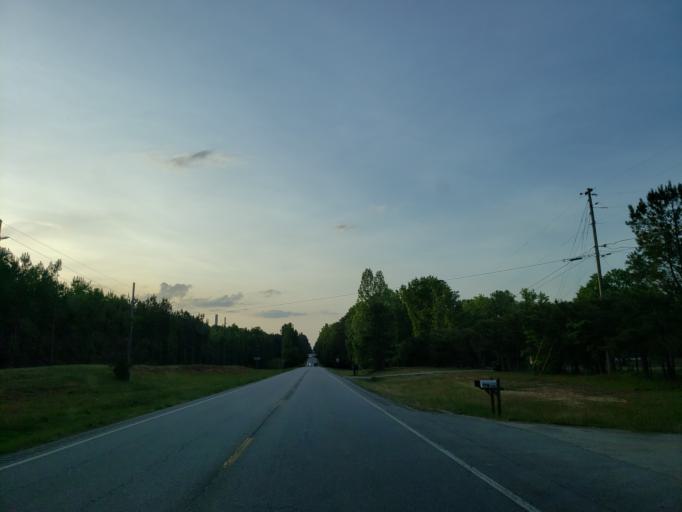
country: US
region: Georgia
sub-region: Coweta County
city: Newnan
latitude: 33.4407
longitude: -84.8764
